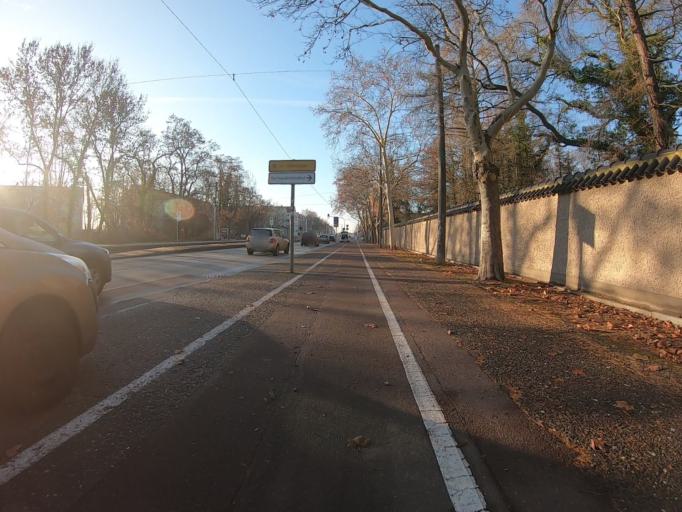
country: DE
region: Saxony-Anhalt
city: Halle (Saale)
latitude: 51.5052
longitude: 11.9896
